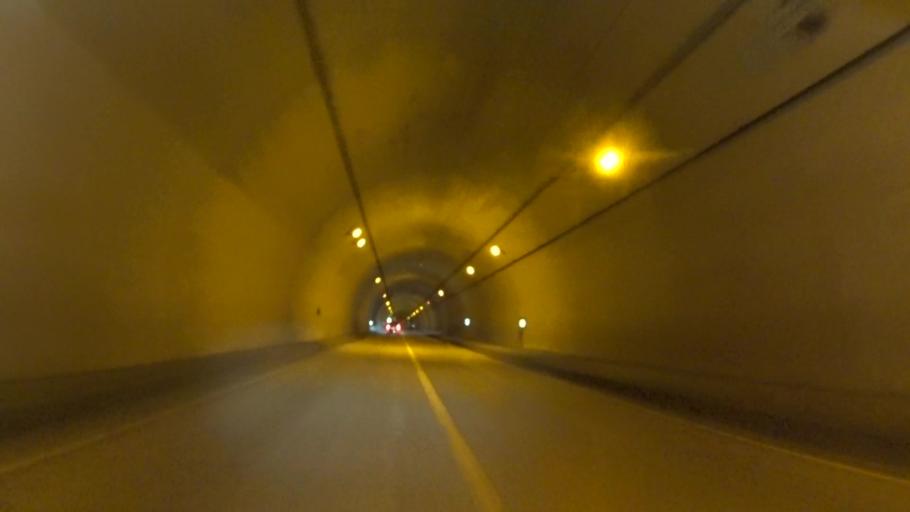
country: JP
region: Kyoto
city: Fukuchiyama
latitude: 35.4012
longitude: 135.0383
